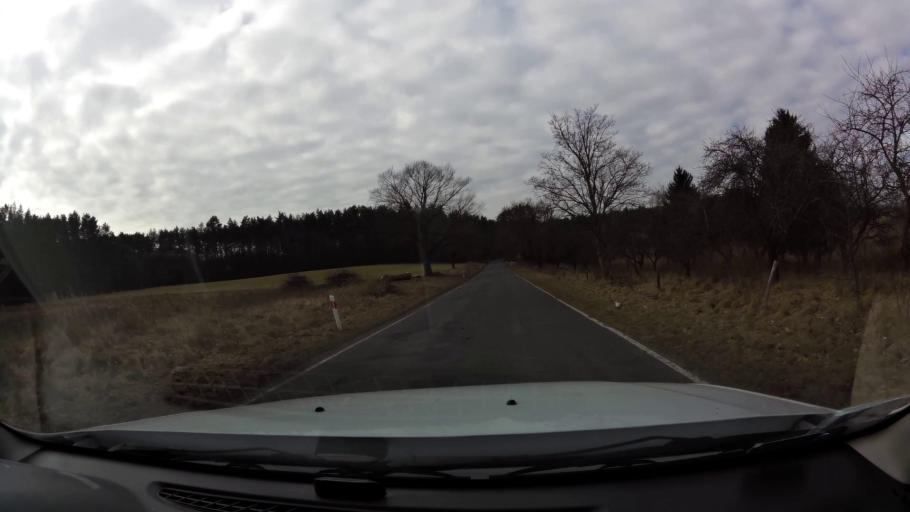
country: PL
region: West Pomeranian Voivodeship
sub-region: Powiat mysliborski
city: Debno
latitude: 52.7139
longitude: 14.6718
